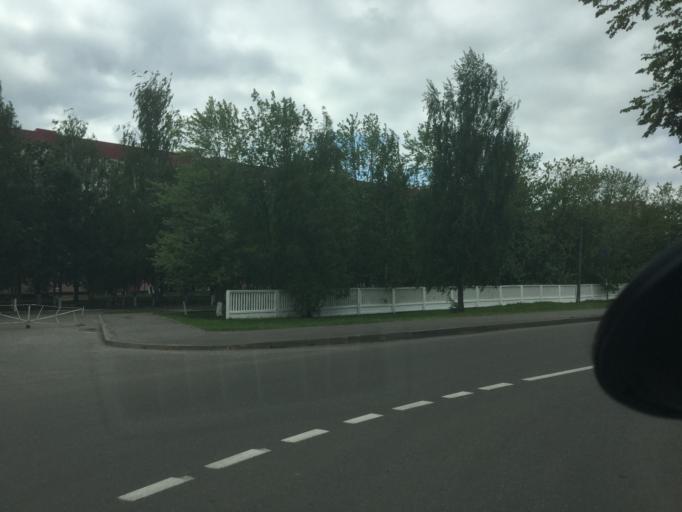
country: BY
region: Vitebsk
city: Vitebsk
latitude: 55.1598
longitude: 30.2267
